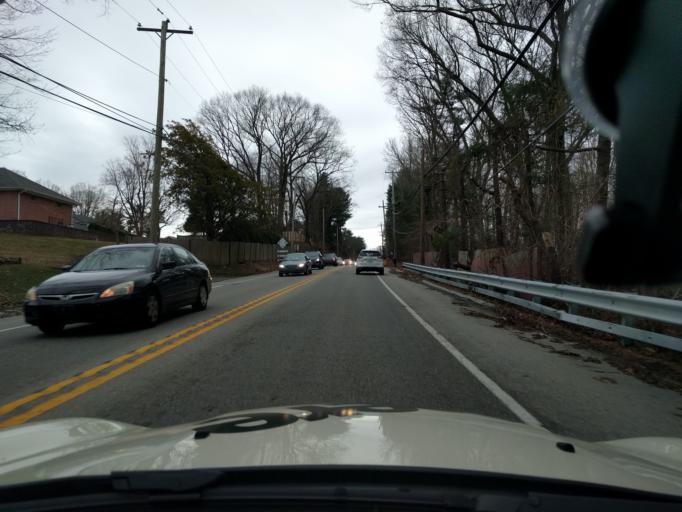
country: US
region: Pennsylvania
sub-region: Delaware County
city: Media
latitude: 39.9480
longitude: -75.3950
